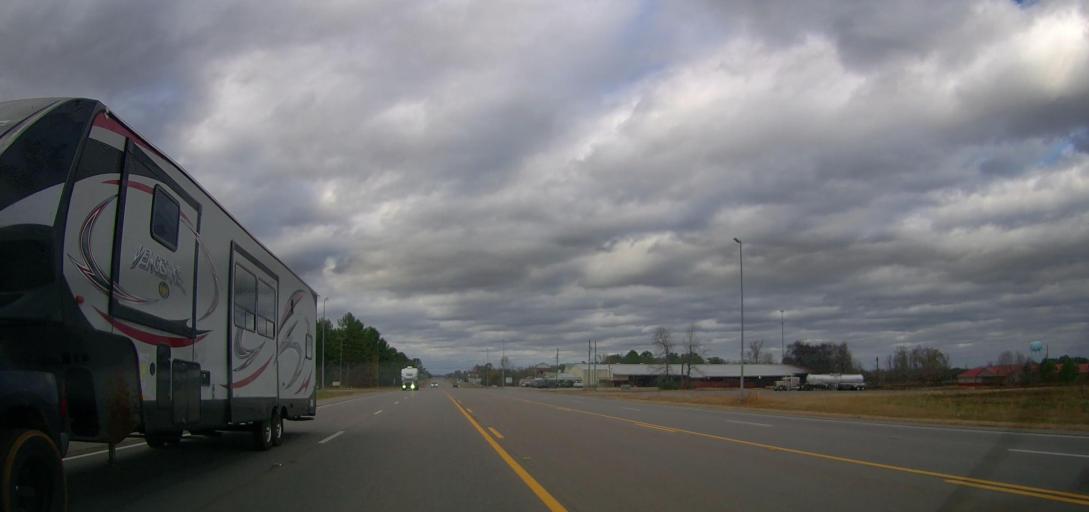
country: US
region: Alabama
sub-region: Lawrence County
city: Moulton
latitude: 34.5022
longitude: -87.2845
